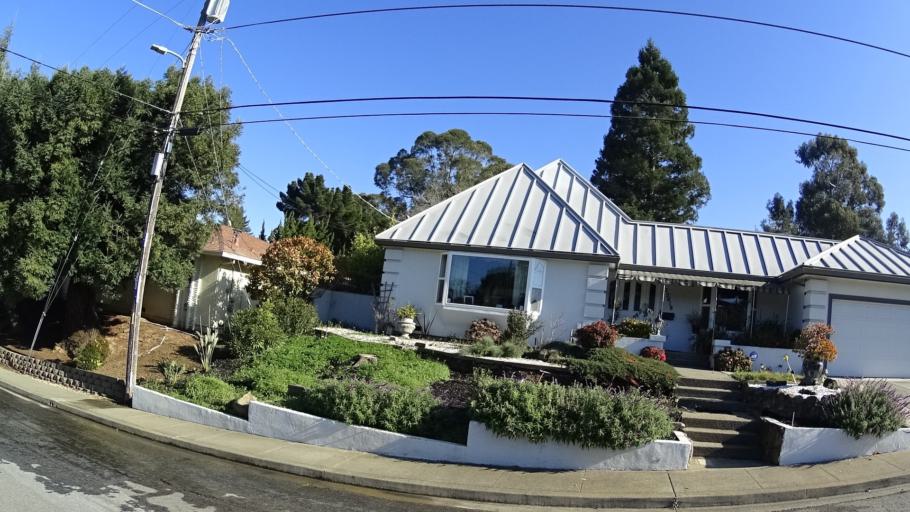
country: US
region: California
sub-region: Alameda County
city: Fairview
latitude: 37.6684
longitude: -122.0458
